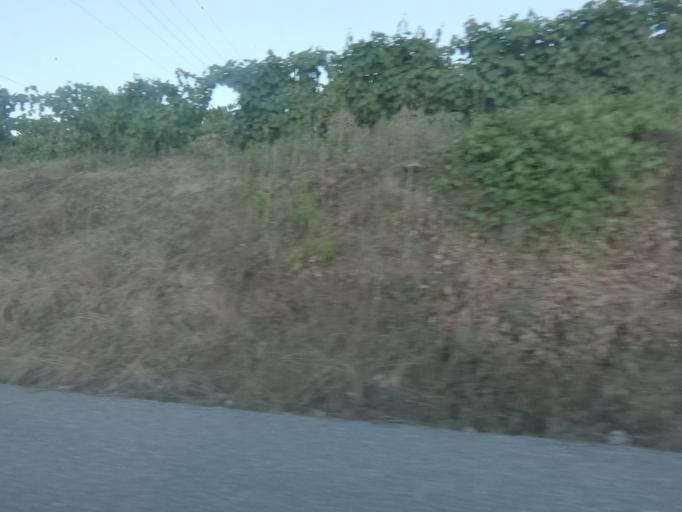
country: PT
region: Vila Real
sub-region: Peso da Regua
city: Peso da Regua
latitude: 41.1344
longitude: -7.7442
